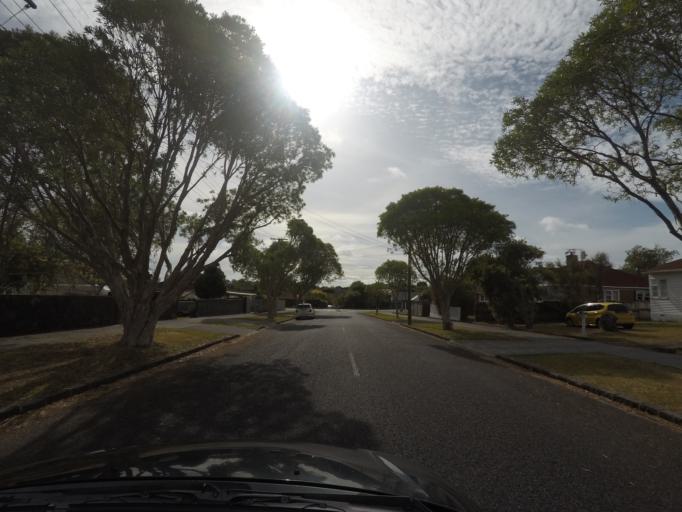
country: NZ
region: Auckland
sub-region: Auckland
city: Rosebank
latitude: -36.8777
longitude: 174.7153
